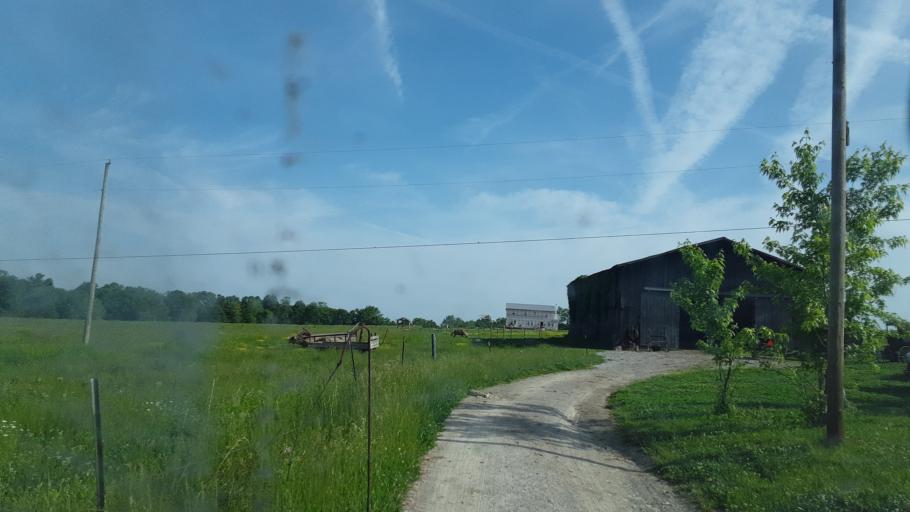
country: US
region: Kentucky
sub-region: Lewis County
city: Vanceburg
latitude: 38.4691
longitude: -83.4960
